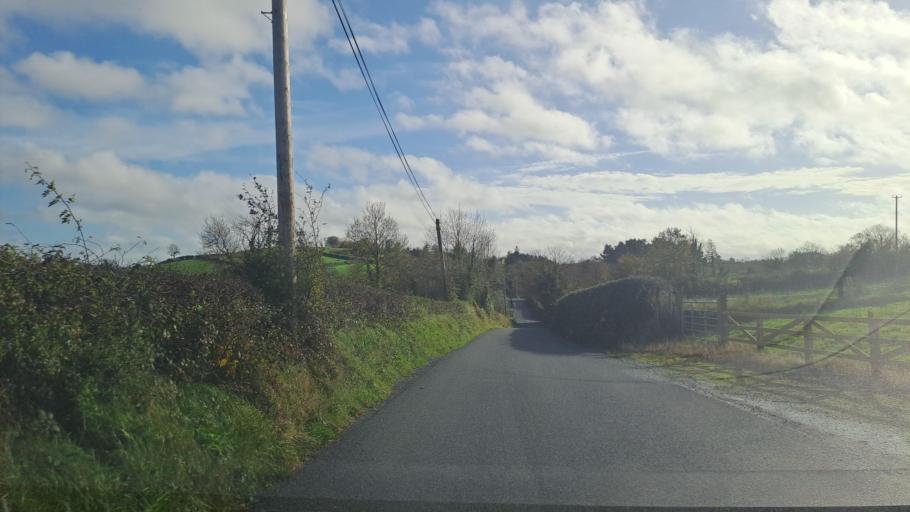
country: IE
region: Ulster
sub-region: An Cabhan
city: Bailieborough
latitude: 53.9908
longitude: -7.0173
